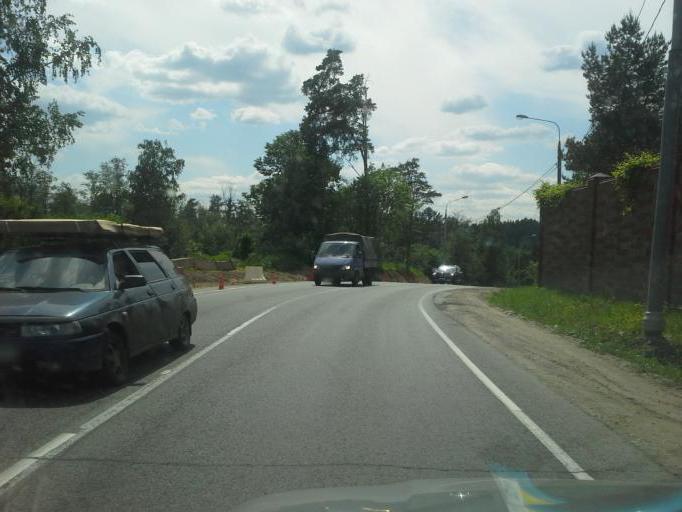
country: RU
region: Moskovskaya
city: Barvikha
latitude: 55.7198
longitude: 37.2683
